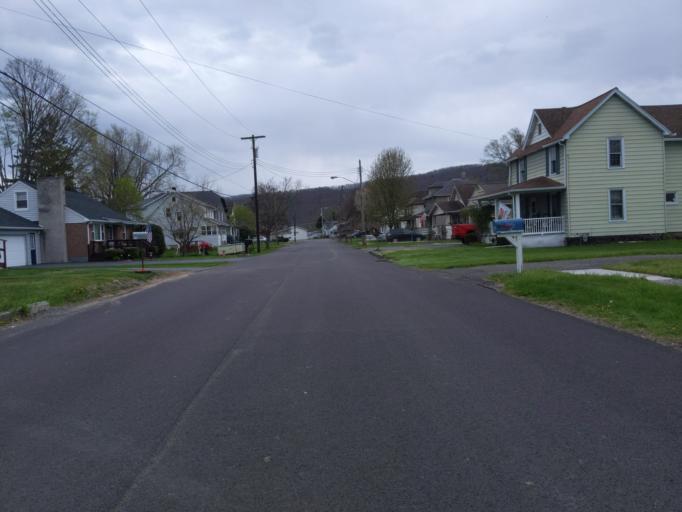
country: US
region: New York
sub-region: Chemung County
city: Southport
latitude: 42.0627
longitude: -76.8109
